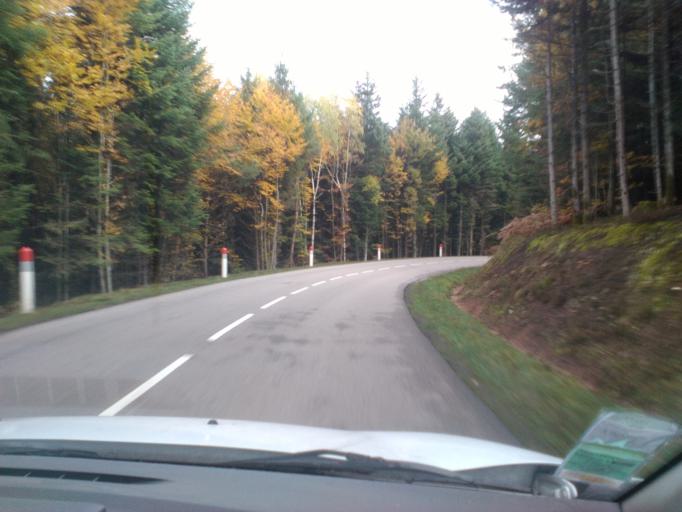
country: FR
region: Lorraine
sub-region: Departement des Vosges
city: Etival-Clairefontaine
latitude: 48.3819
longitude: 6.7867
